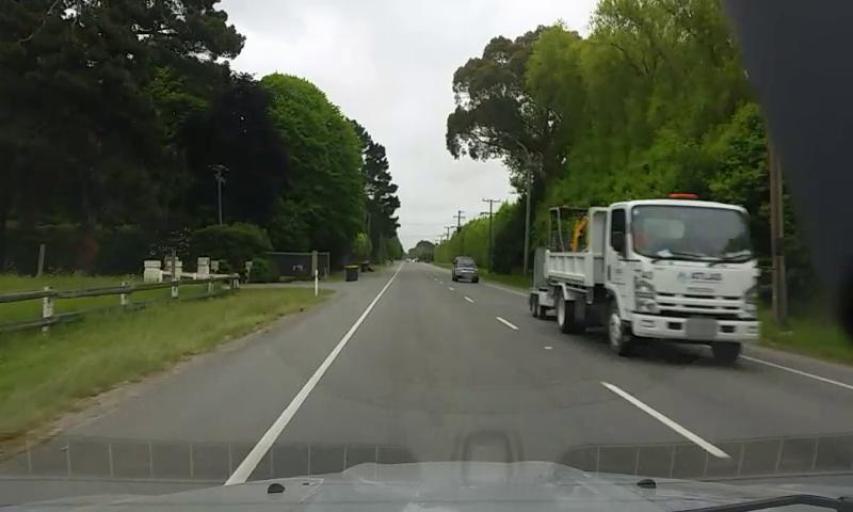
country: NZ
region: Canterbury
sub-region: Selwyn District
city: Prebbleton
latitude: -43.5168
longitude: 172.5227
